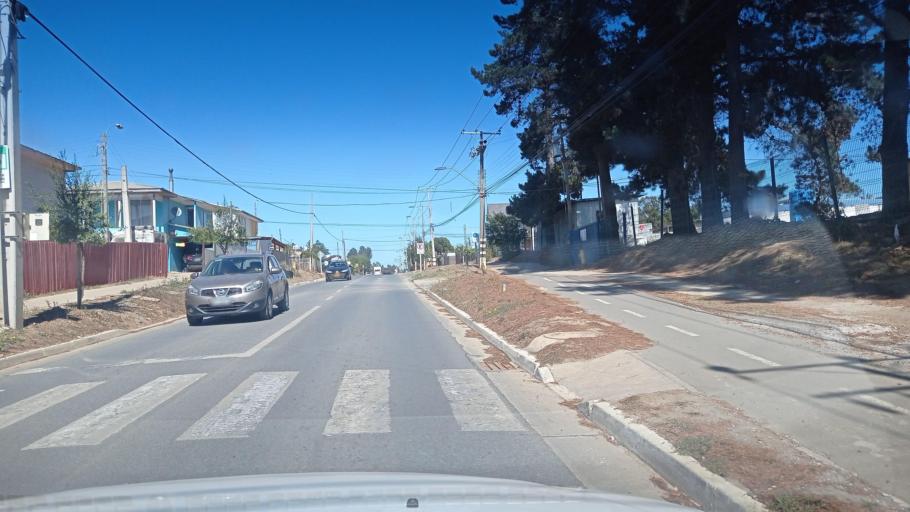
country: CL
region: O'Higgins
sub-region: Provincia de Colchagua
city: Santa Cruz
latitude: -34.4007
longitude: -71.9957
